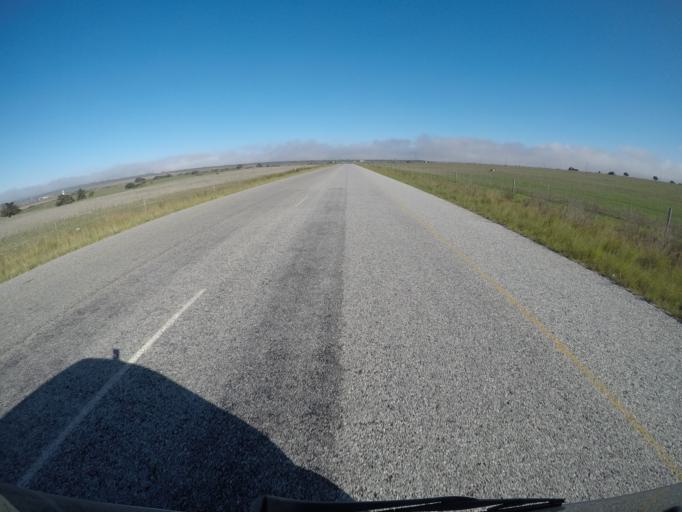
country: ZA
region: Western Cape
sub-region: Eden District Municipality
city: Mossel Bay
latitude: -34.1766
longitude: 22.0160
